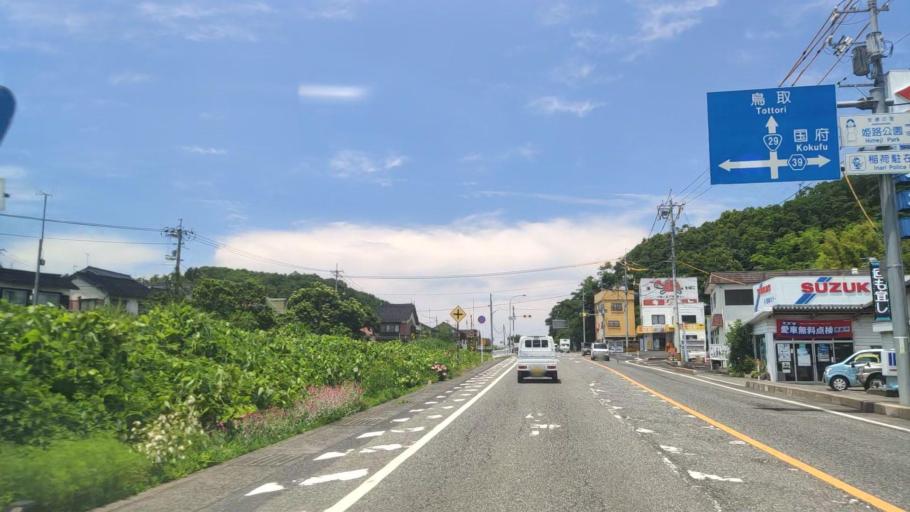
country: JP
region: Tottori
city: Tottori
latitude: 35.4268
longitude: 134.2611
